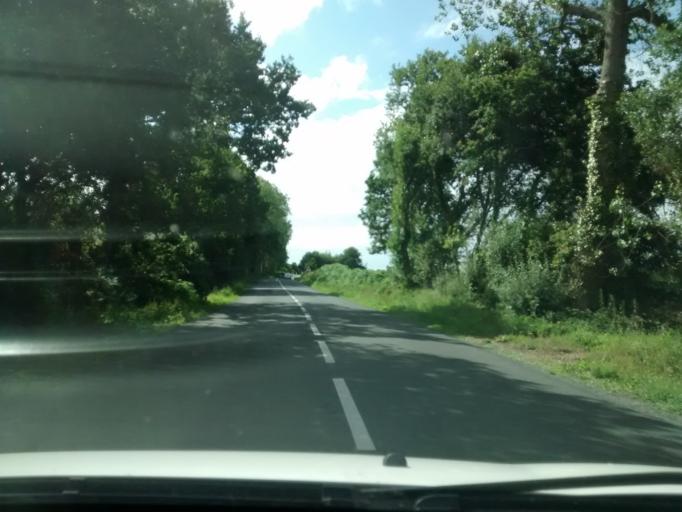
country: FR
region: Brittany
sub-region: Departement des Cotes-d'Armor
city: Penvenan
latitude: 48.7925
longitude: -3.2766
